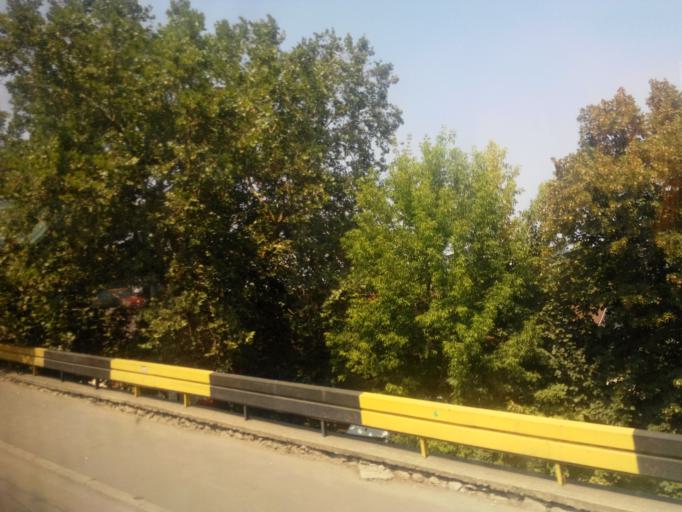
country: RO
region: Cluj
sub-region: Municipiul Cluj-Napoca
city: Cluj-Napoca
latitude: 46.7839
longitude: 23.5843
